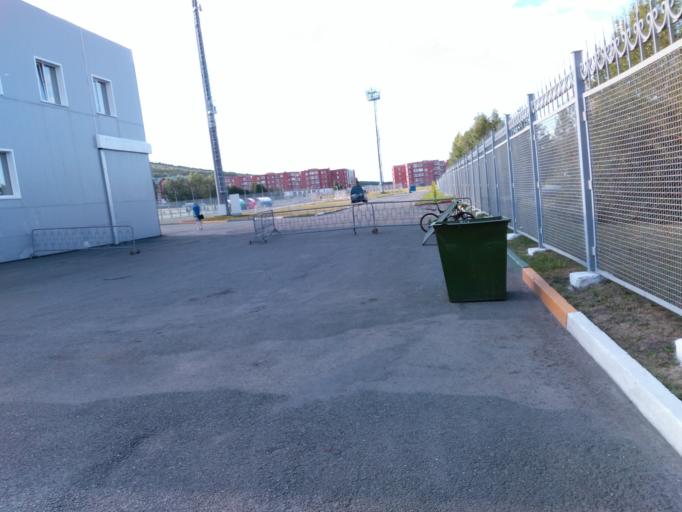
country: RU
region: Bashkortostan
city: Uchaly
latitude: 54.3199
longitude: 59.3716
